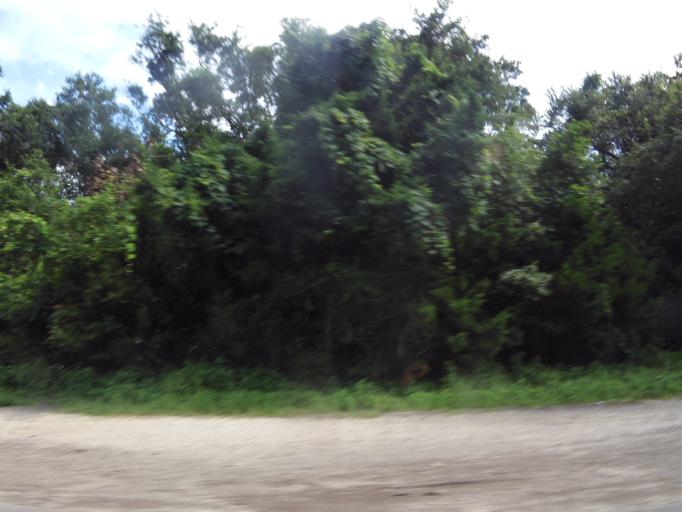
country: US
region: Florida
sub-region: Nassau County
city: Fernandina Beach
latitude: 30.6776
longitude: -81.4516
